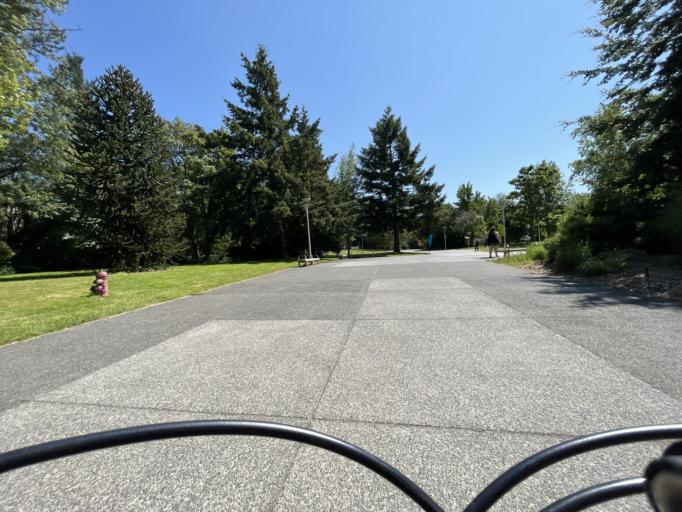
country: CA
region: British Columbia
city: Oak Bay
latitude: 48.4626
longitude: -123.3131
